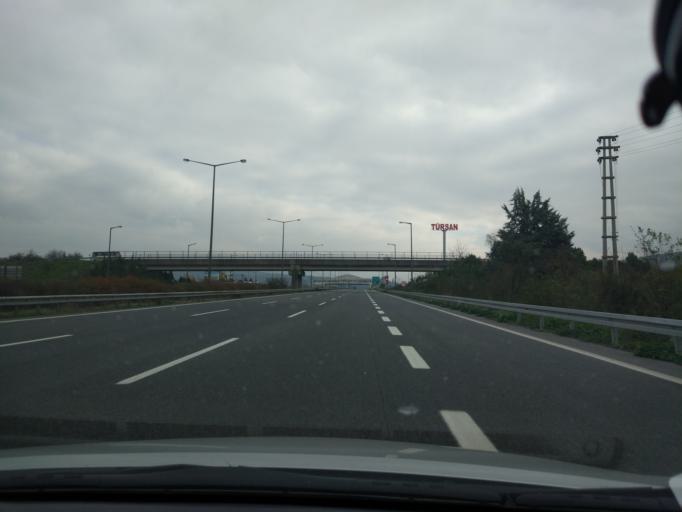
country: TR
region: Duzce
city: Duzce
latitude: 40.7906
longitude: 31.2337
